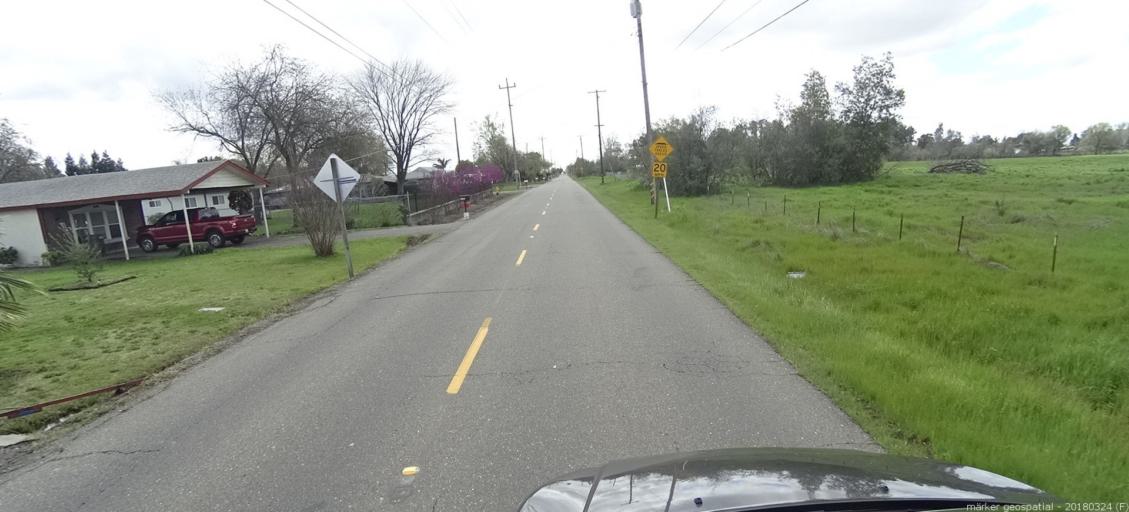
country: US
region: California
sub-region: Sacramento County
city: North Highlands
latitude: 38.6893
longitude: -121.3875
